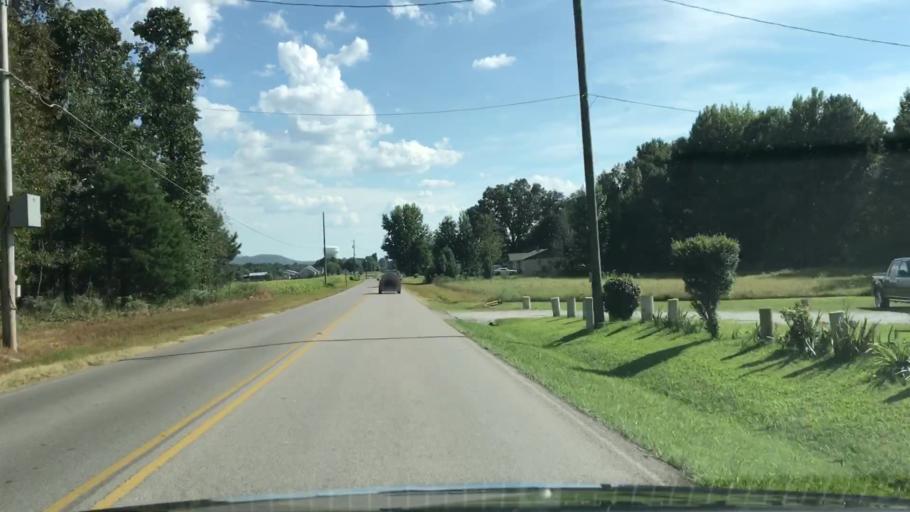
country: US
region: Alabama
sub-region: Madison County
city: Harvest
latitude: 34.8740
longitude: -86.7489
